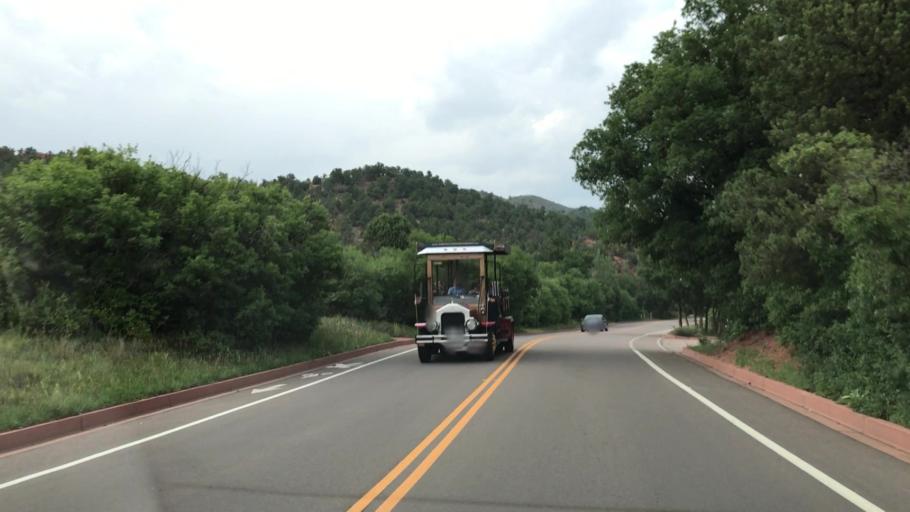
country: US
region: Colorado
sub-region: El Paso County
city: Manitou Springs
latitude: 38.8718
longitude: -104.8851
